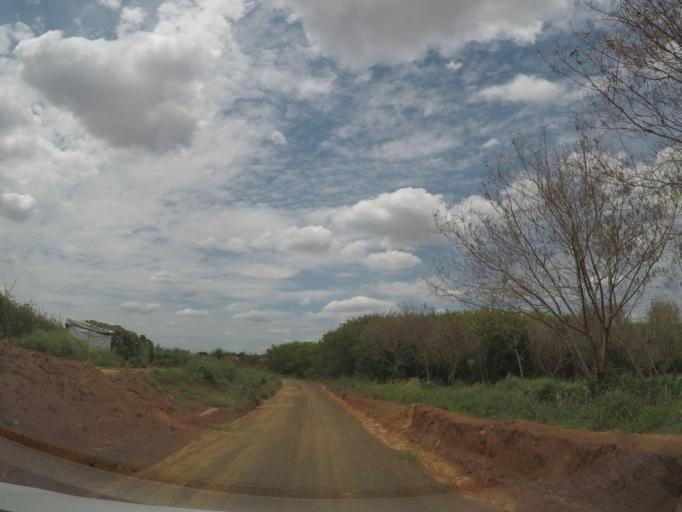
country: BR
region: Sao Paulo
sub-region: Sumare
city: Sumare
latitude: -22.8373
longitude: -47.2840
